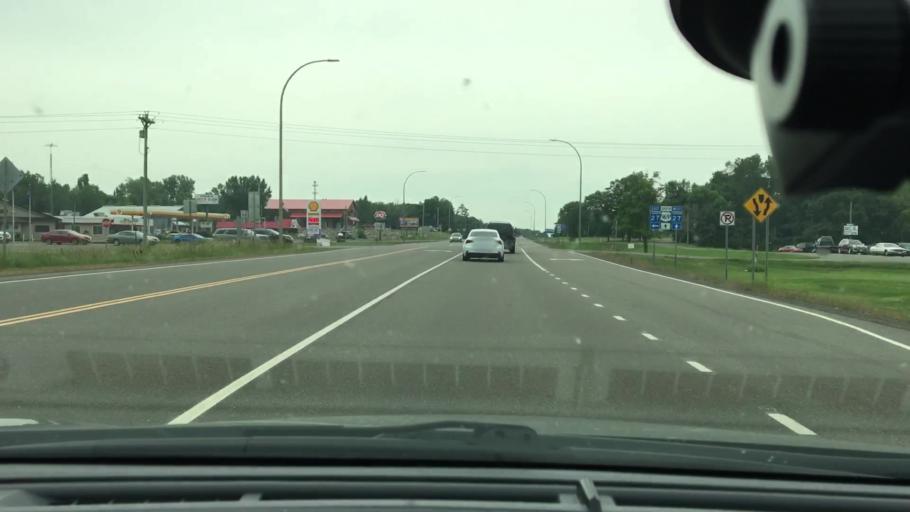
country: US
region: Minnesota
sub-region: Mille Lacs County
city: Vineland
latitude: 46.1096
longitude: -93.6454
